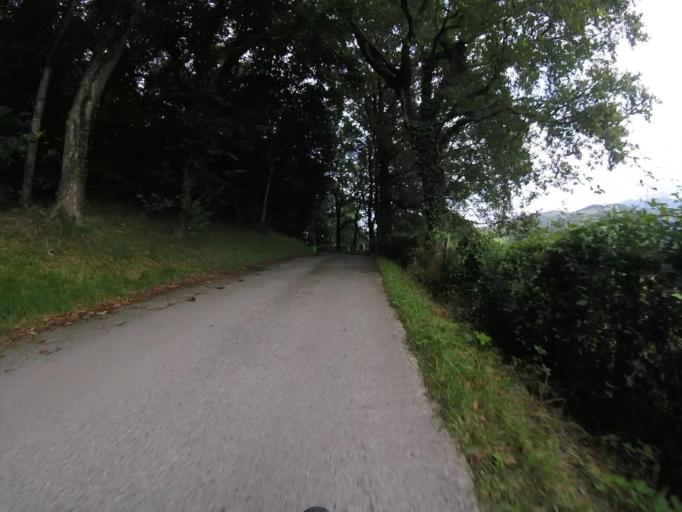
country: ES
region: Basque Country
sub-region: Provincia de Guipuzcoa
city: Lezo
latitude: 43.3035
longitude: -1.8542
